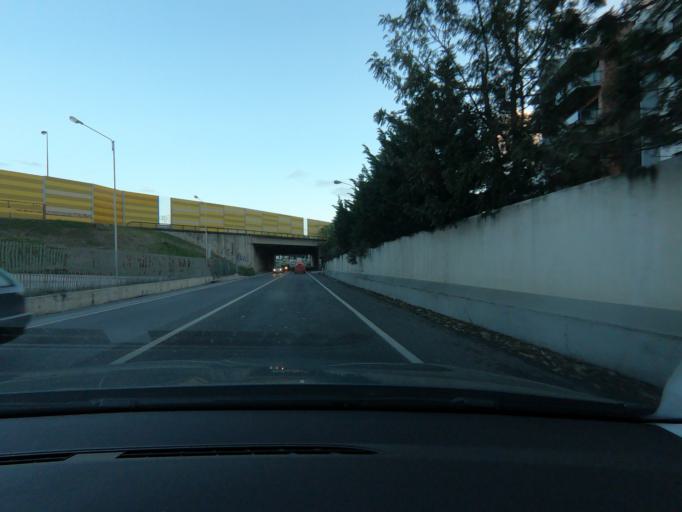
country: PT
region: Lisbon
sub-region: Vila Franca de Xira
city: Vila Franca de Xira
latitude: 38.9708
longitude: -8.9825
